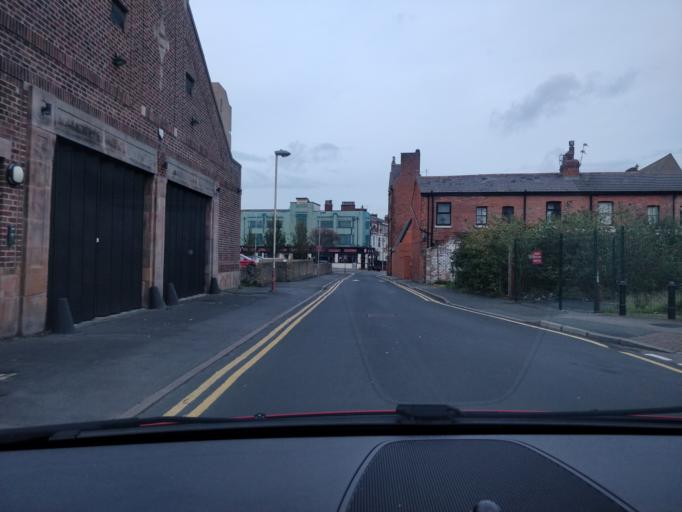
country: GB
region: England
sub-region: Sefton
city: Southport
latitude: 53.6491
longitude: -3.0071
